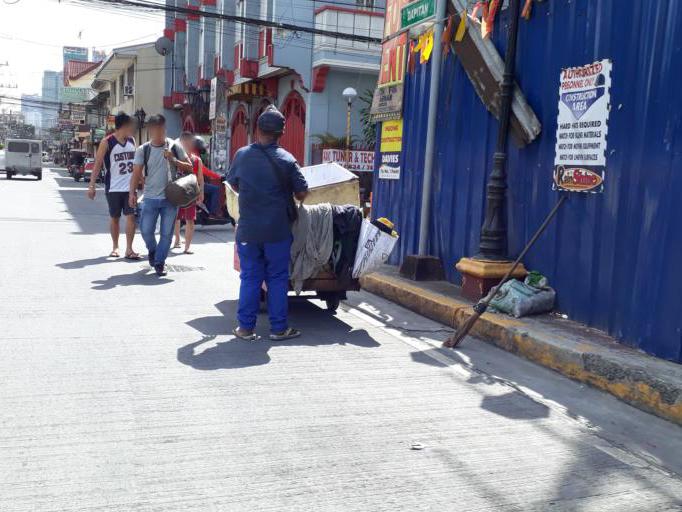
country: PH
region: Metro Manila
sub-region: City of Manila
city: Manila
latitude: 14.6174
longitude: 120.9946
